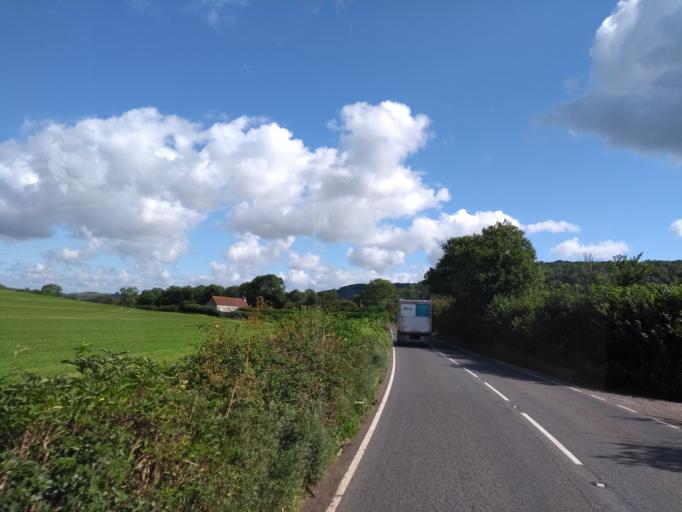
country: GB
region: England
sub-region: Somerset
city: Street
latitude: 51.0716
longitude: -2.7250
